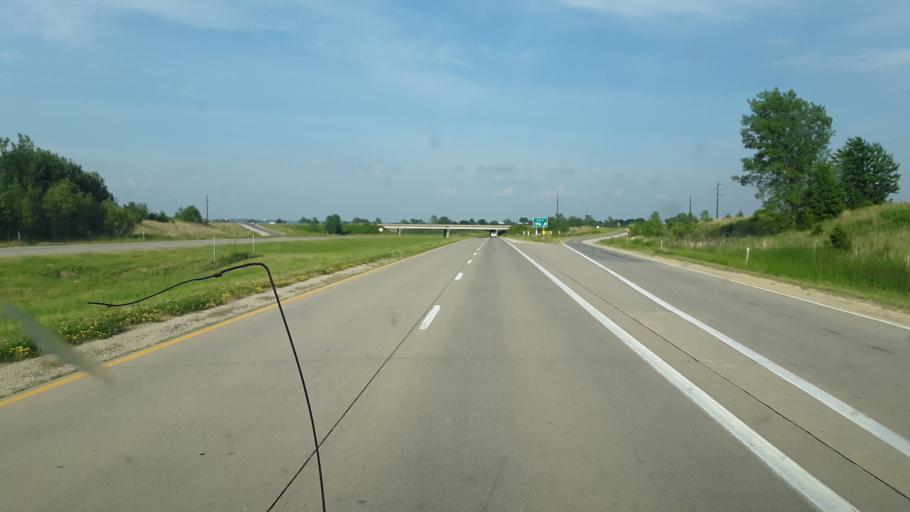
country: US
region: Iowa
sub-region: Marshall County
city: Marshalltown
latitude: 42.0029
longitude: -92.8893
